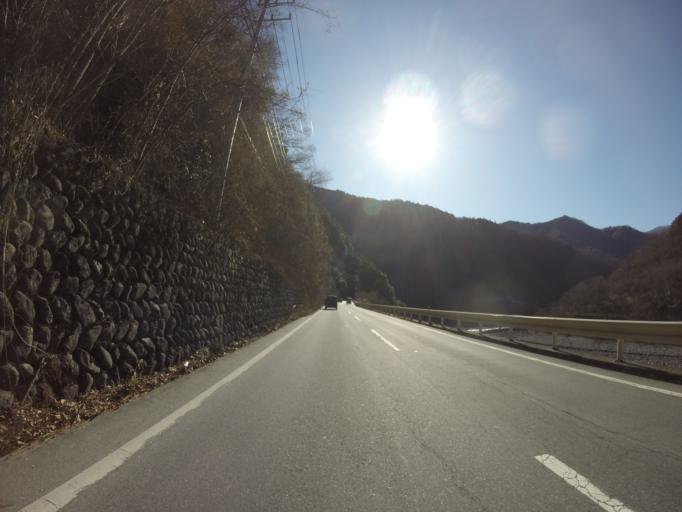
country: JP
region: Yamanashi
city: Ryuo
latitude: 35.4284
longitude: 138.4094
